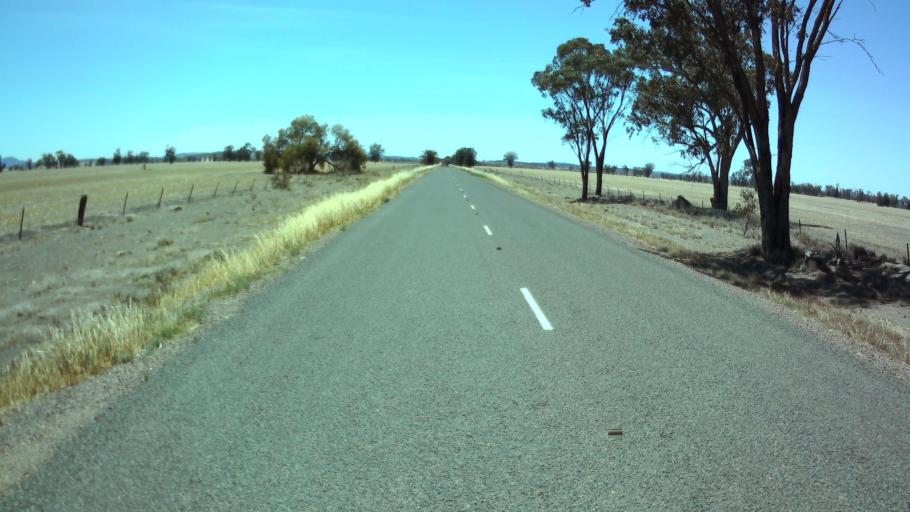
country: AU
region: New South Wales
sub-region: Bland
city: West Wyalong
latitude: -33.6595
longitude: 147.5936
